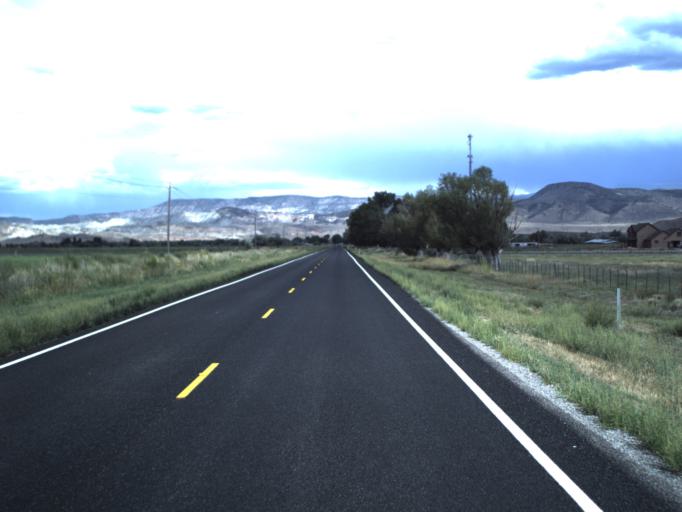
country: US
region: Utah
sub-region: Sevier County
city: Richfield
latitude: 38.7730
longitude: -112.0525
